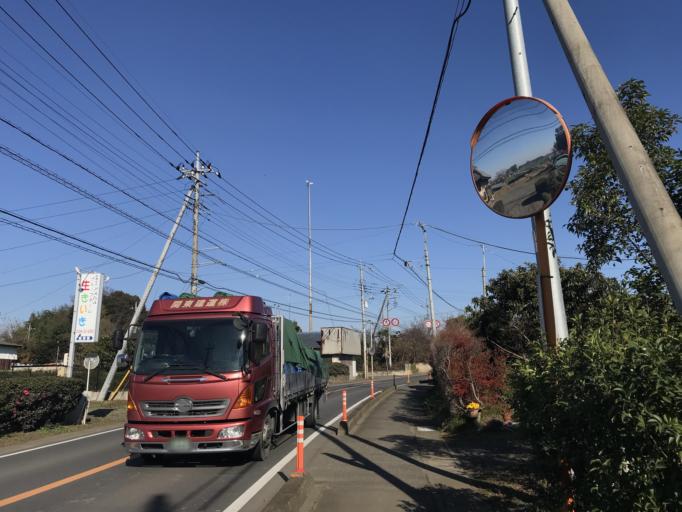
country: JP
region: Tochigi
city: Oyama
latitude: 36.2646
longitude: 139.8409
